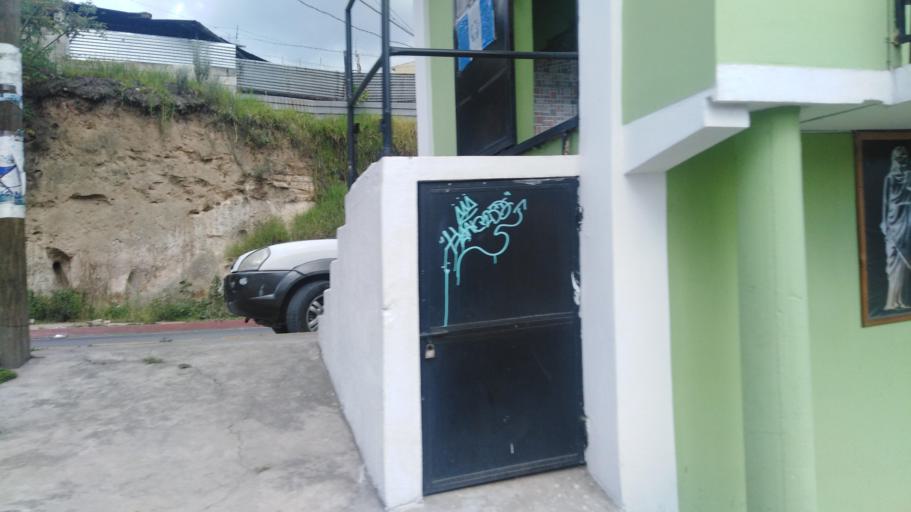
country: GT
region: Quetzaltenango
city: Quetzaltenango
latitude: 14.8520
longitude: -91.5122
